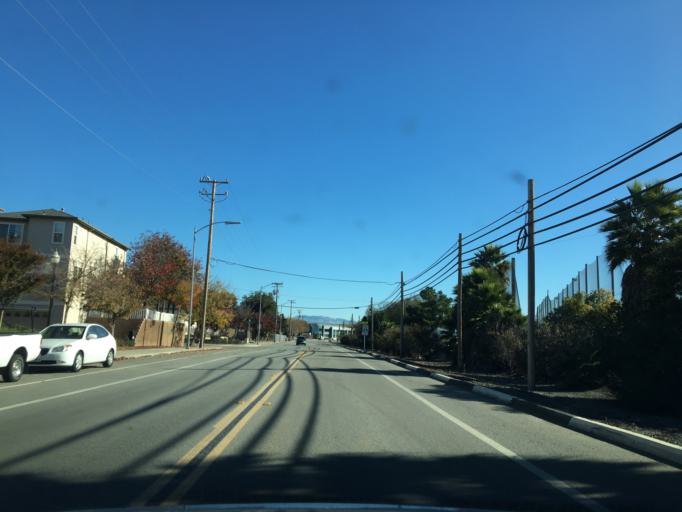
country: US
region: California
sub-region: Santa Clara County
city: Milpitas
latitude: 37.4247
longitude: -121.9707
